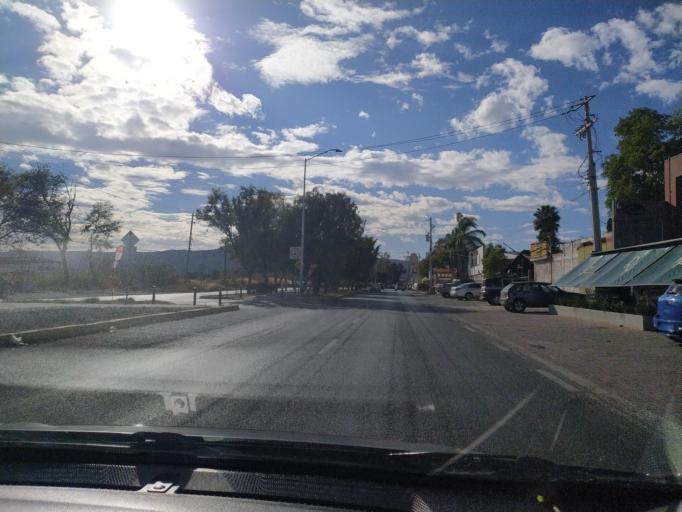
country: LA
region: Oudomxai
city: Muang La
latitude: 21.0289
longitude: 101.8493
